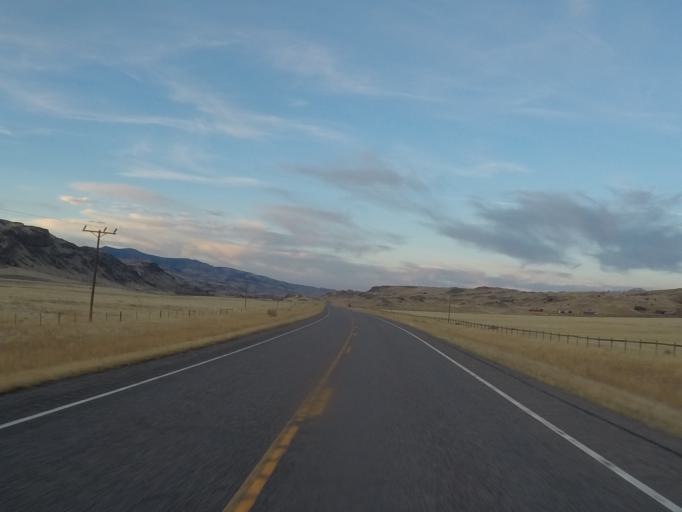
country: US
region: Montana
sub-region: Gallatin County
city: Bozeman
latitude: 45.2216
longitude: -110.8823
